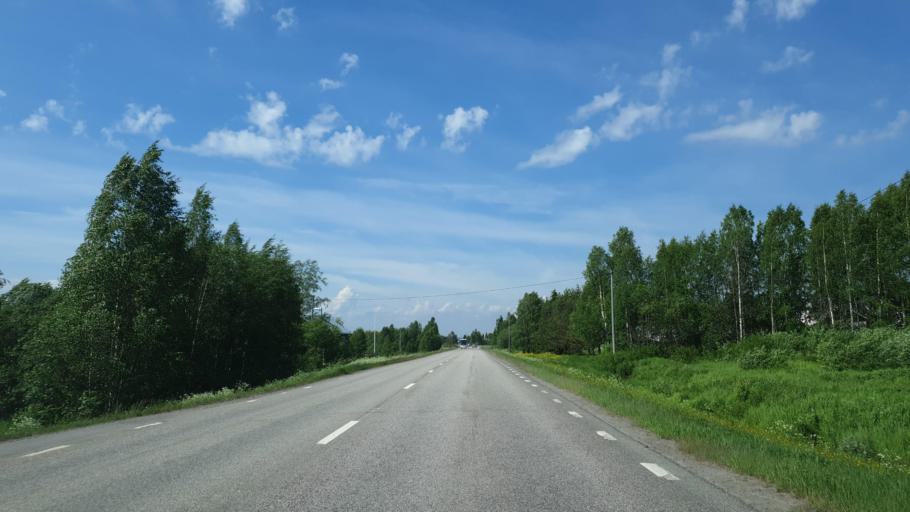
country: SE
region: Norrbotten
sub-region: Pitea Kommun
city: Rosvik
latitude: 65.5630
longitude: 21.7888
